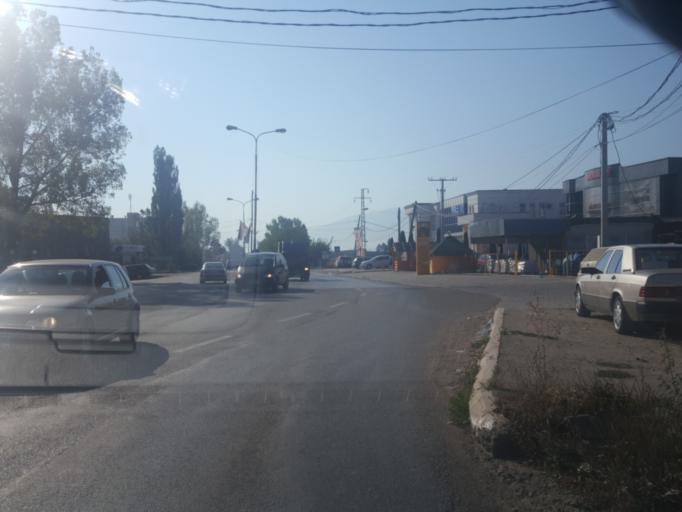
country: XK
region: Gjakova
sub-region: Komuna e Gjakoves
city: Gjakove
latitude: 42.3980
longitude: 20.4186
